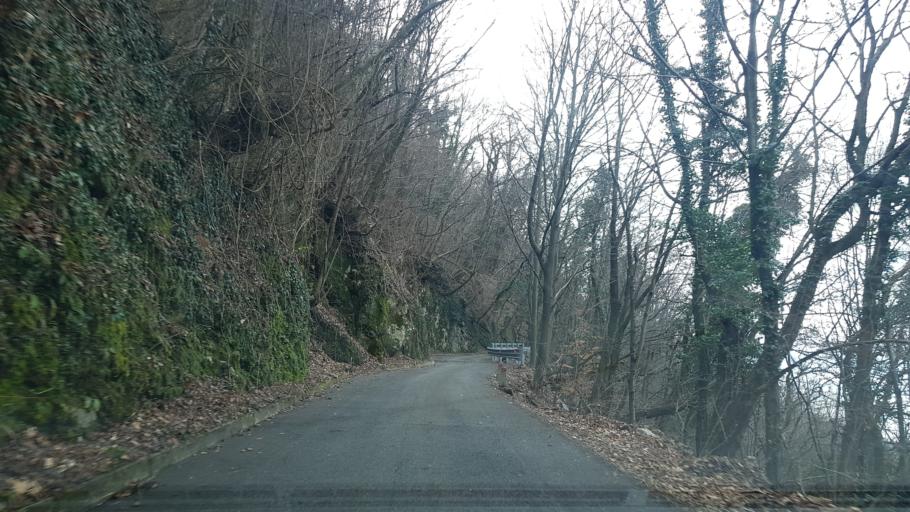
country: IT
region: Friuli Venezia Giulia
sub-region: Provincia di Udine
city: Clodig
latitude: 46.1767
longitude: 13.5781
